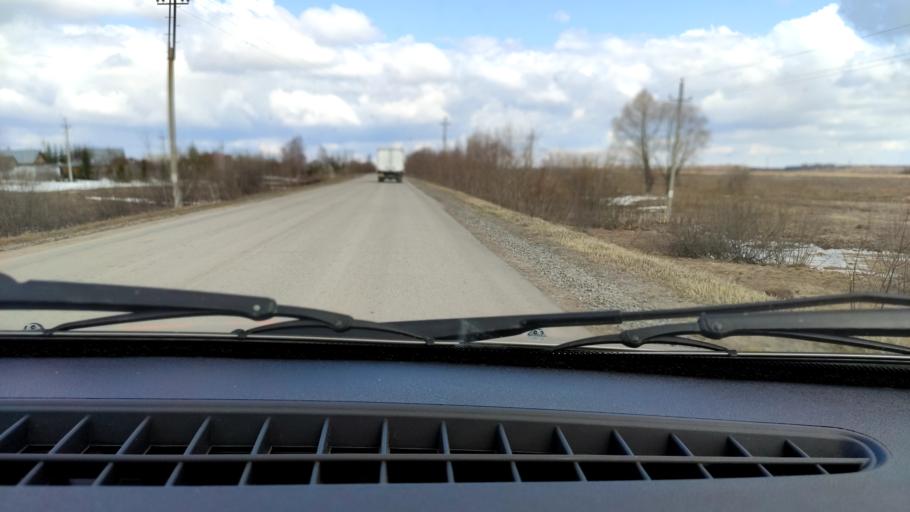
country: RU
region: Bashkortostan
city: Kudeyevskiy
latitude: 54.8291
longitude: 56.7932
